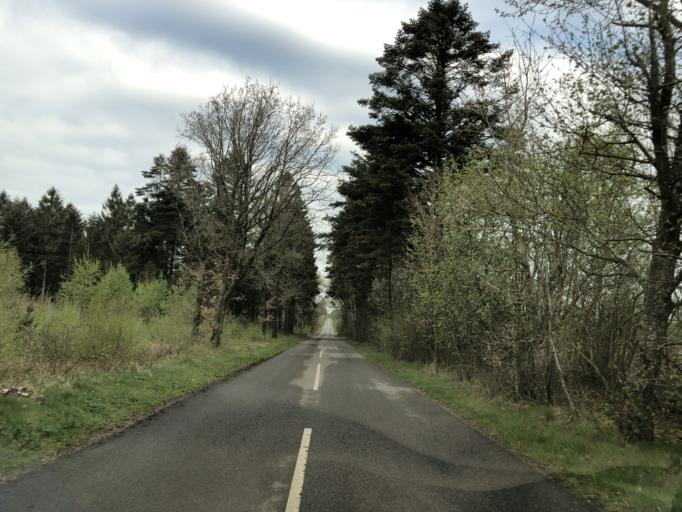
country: DK
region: Central Jutland
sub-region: Holstebro Kommune
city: Holstebro
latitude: 56.3143
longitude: 8.5241
